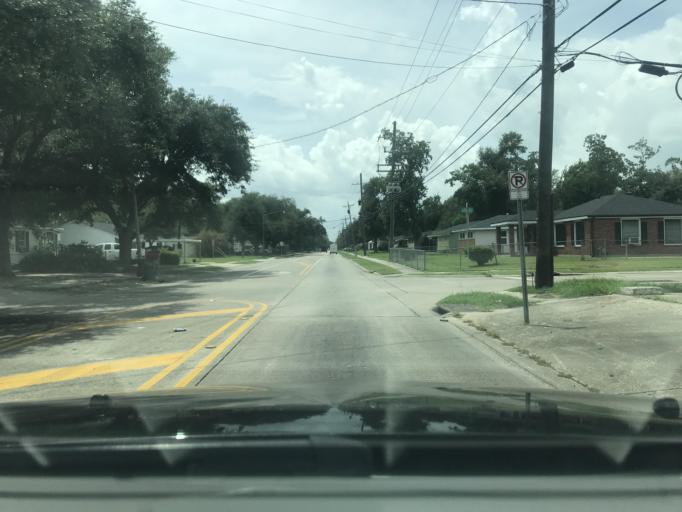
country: US
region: Louisiana
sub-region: Calcasieu Parish
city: Lake Charles
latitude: 30.2131
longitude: -93.1884
